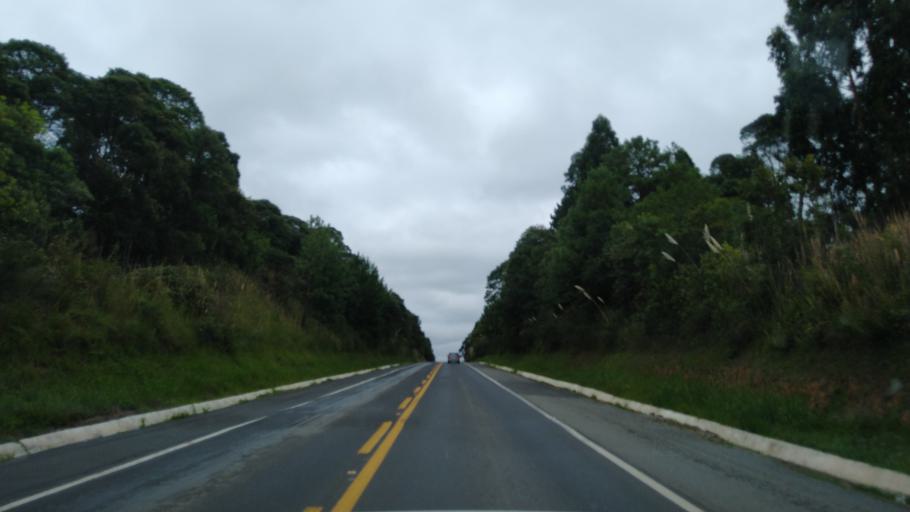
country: BR
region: Santa Catarina
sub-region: Tres Barras
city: Tres Barras
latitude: -26.1706
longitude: -50.1539
